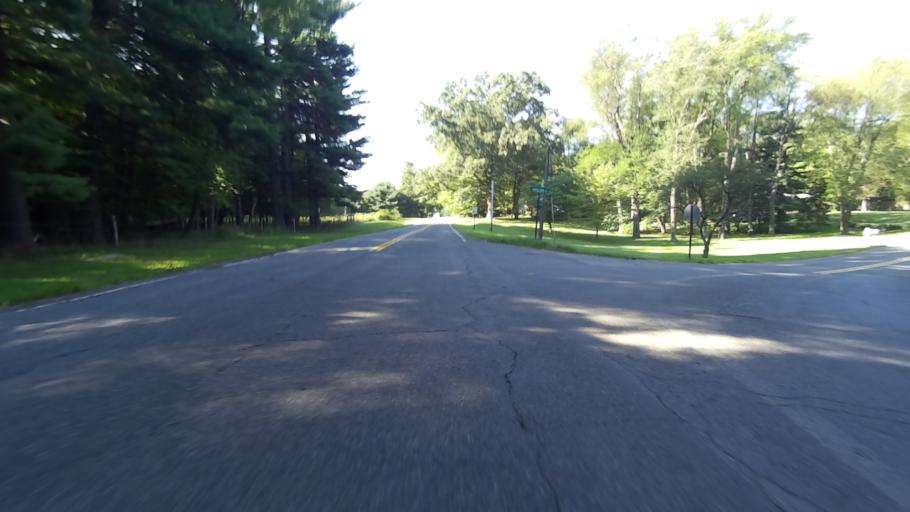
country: US
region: Ohio
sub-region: Portage County
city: Kent
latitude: 41.1912
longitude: -81.3330
